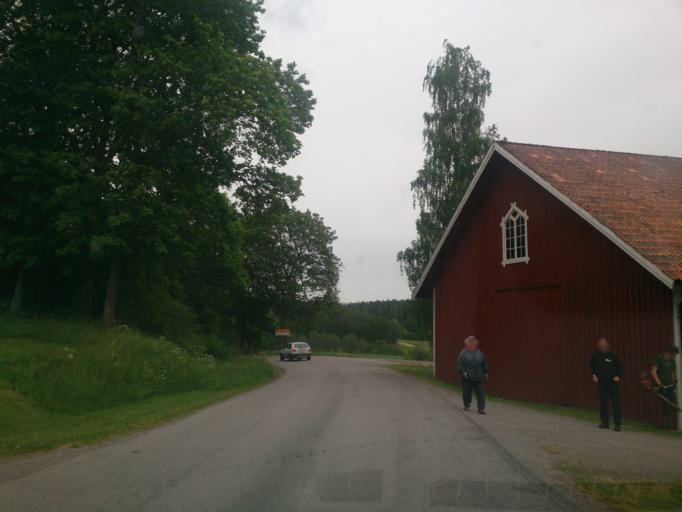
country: SE
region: OEstergoetland
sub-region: Valdemarsviks Kommun
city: Gusum
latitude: 58.3122
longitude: 16.3389
